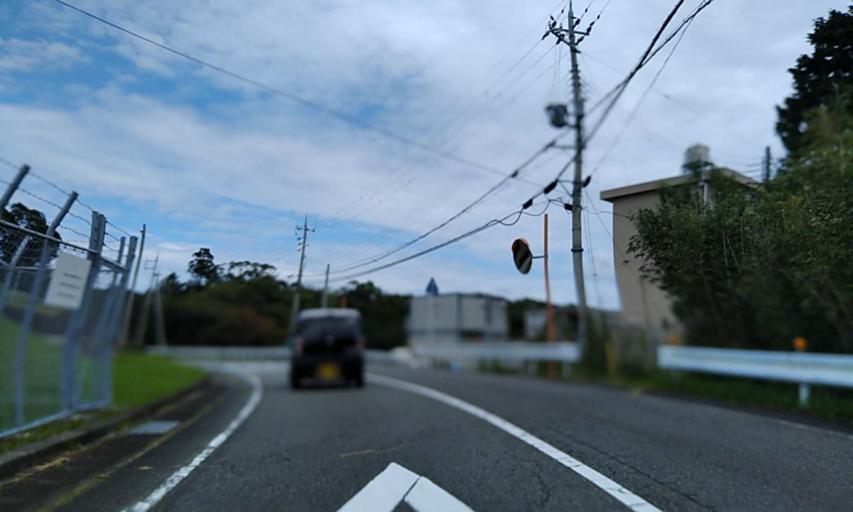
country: JP
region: Wakayama
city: Shingu
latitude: 33.4666
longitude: 135.8301
